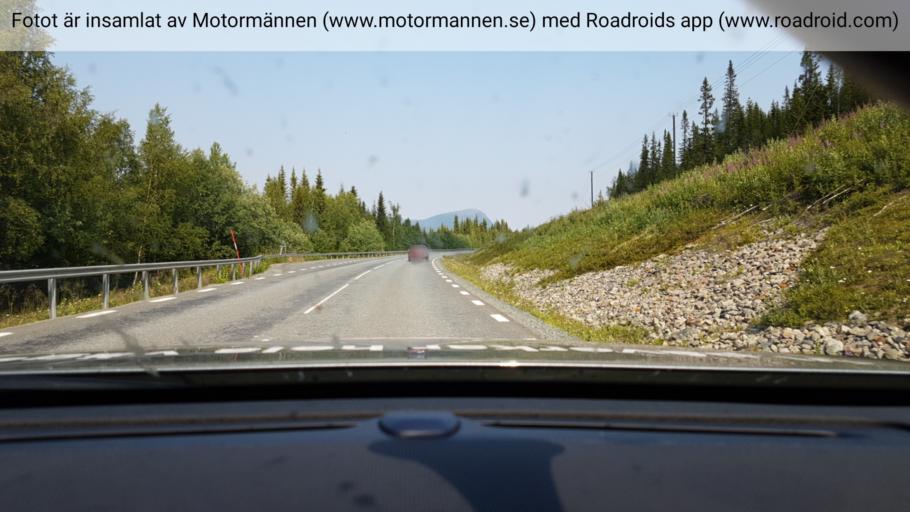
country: SE
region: Vaesterbotten
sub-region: Vilhelmina Kommun
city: Sjoberg
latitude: 65.5573
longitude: 15.5421
